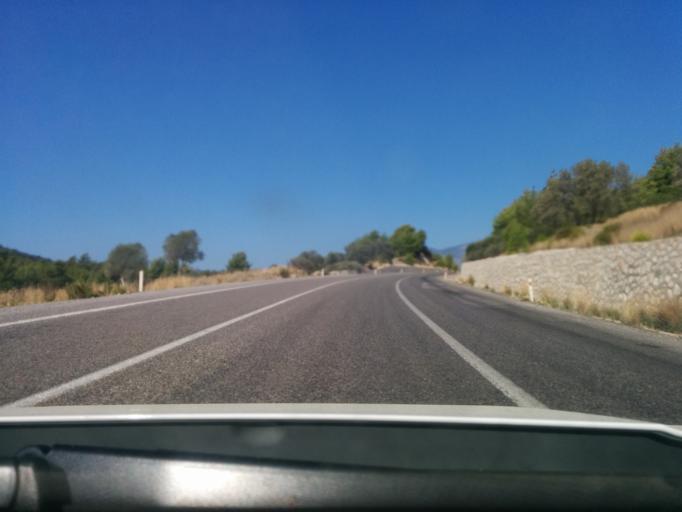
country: TR
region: Mugla
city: Esen
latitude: 36.4015
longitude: 29.3027
